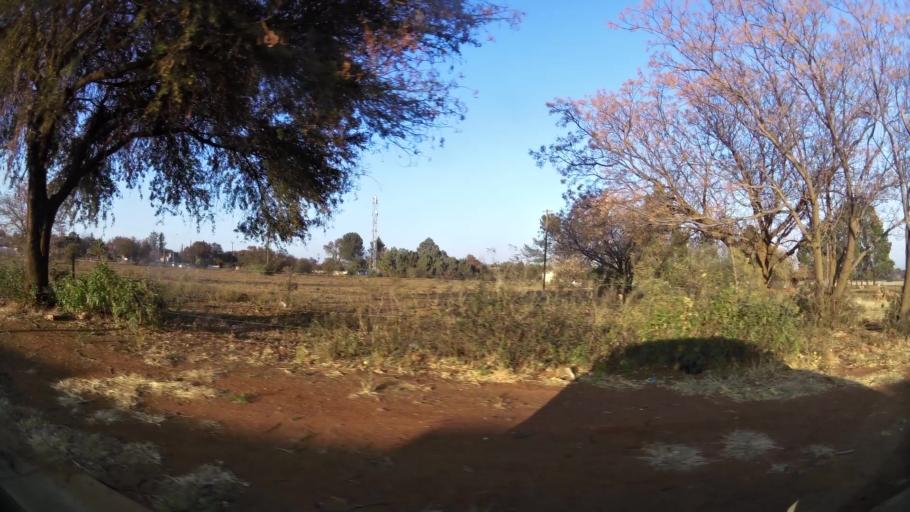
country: ZA
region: Orange Free State
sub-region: Mangaung Metropolitan Municipality
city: Bloemfontein
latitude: -29.0939
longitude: 26.1478
